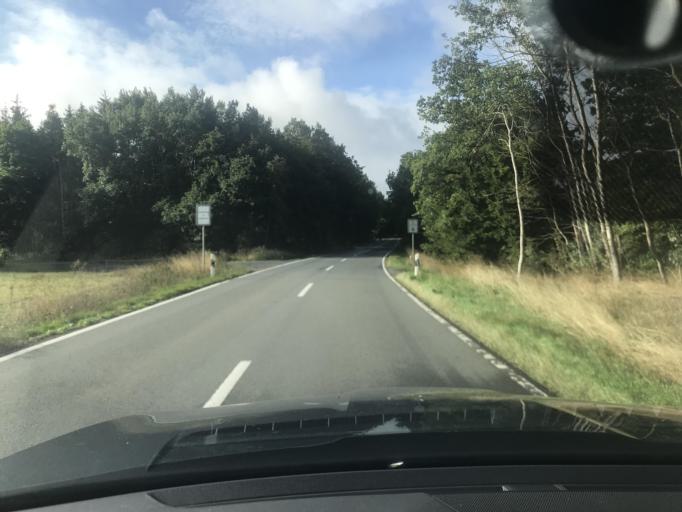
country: DE
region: Saxony-Anhalt
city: Harzgerode
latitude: 51.6042
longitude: 11.0880
